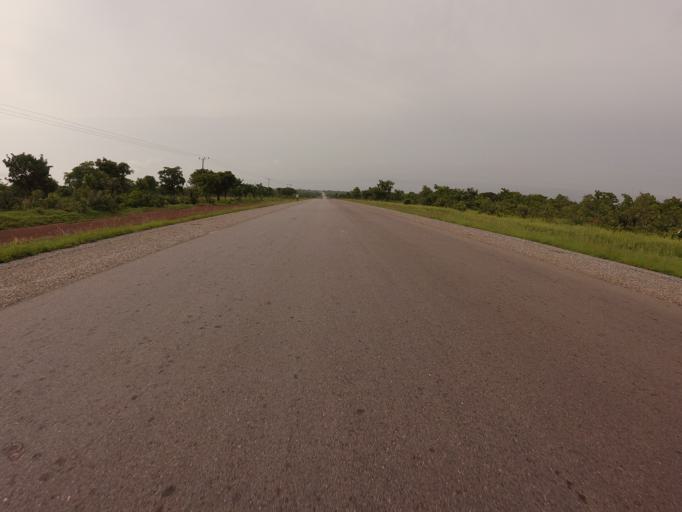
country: GH
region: Northern
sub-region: Yendi
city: Yendi
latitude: 9.6369
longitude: -0.0627
